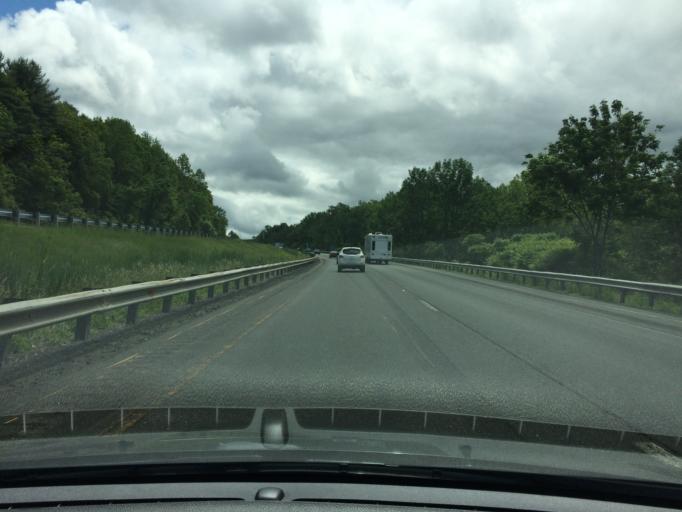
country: US
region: Massachusetts
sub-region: Berkshire County
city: Otis
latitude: 42.2609
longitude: -73.1265
